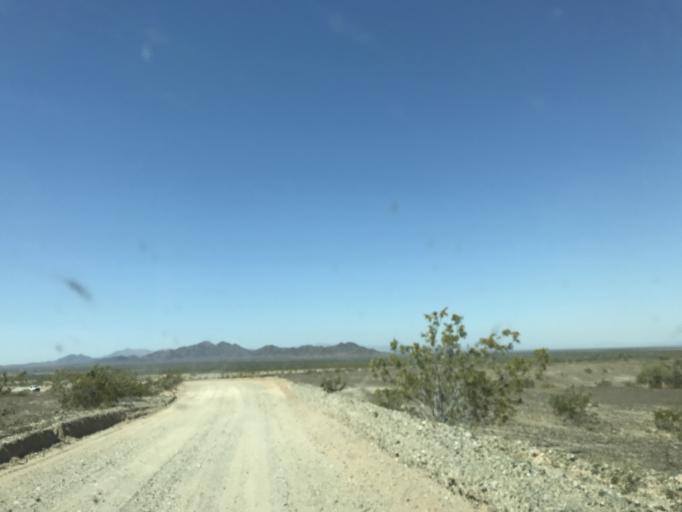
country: US
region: California
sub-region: Riverside County
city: Mesa Verde
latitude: 33.5006
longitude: -114.8580
